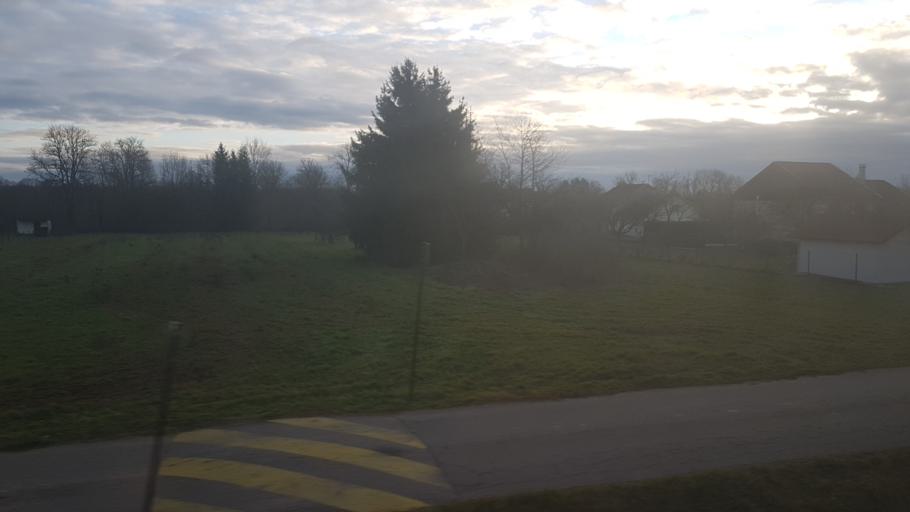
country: FR
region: Lorraine
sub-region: Departement des Vosges
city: Igney
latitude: 48.2771
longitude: 6.3988
